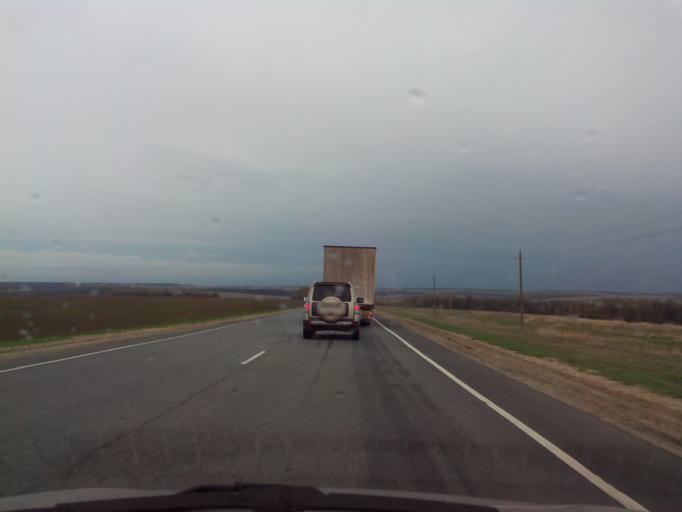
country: RU
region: Moskovskaya
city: Uzunovo
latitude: 54.4866
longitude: 38.5173
